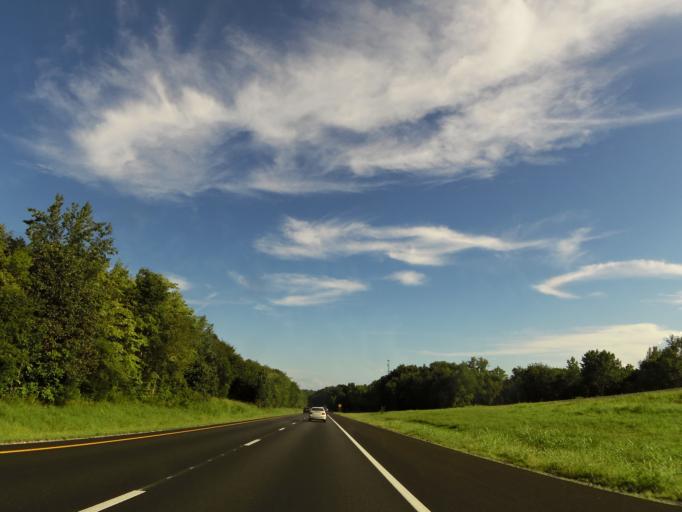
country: US
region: Tennessee
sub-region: Montgomery County
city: Clarksville
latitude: 36.5552
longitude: -87.2498
